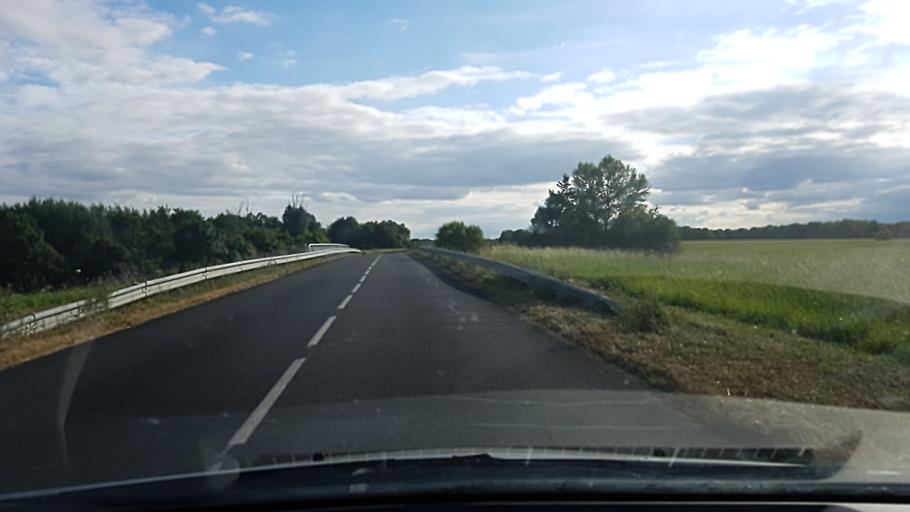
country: FR
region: Pays de la Loire
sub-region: Departement de Maine-et-Loire
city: Maze
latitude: 47.4936
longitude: -0.2722
